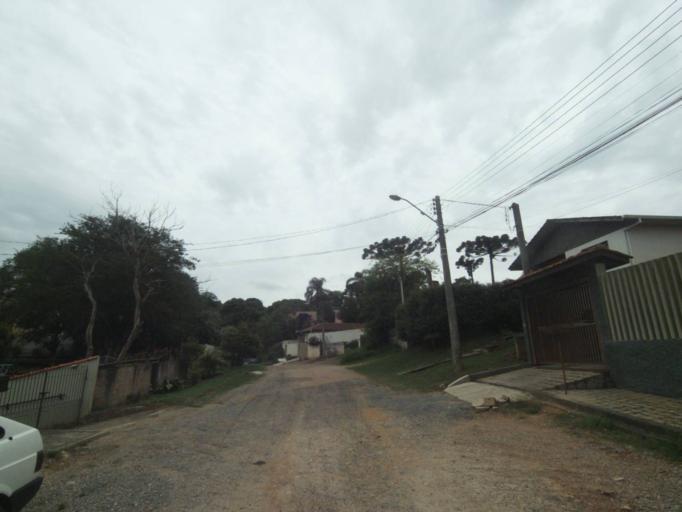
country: BR
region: Parana
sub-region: Curitiba
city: Curitiba
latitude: -25.3989
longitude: -49.2919
